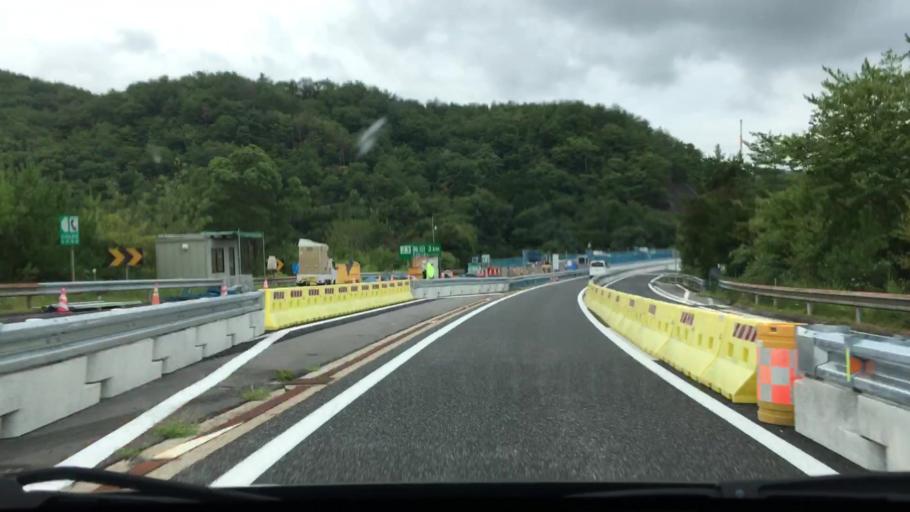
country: JP
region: Hiroshima
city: Miyoshi
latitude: 34.7289
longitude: 132.7036
